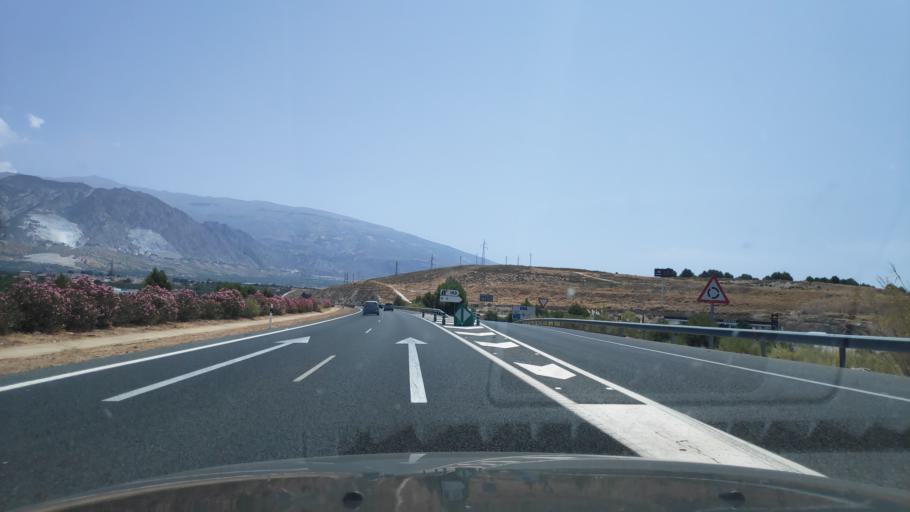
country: ES
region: Andalusia
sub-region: Provincia de Granada
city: Padul
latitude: 36.9884
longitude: -3.6082
